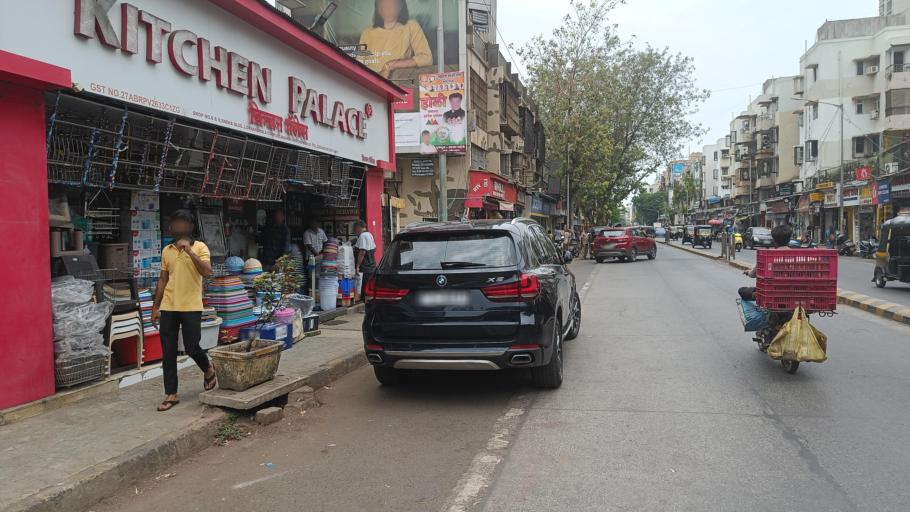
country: IN
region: Maharashtra
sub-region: Mumbai Suburban
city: Powai
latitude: 19.1404
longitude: 72.8260
